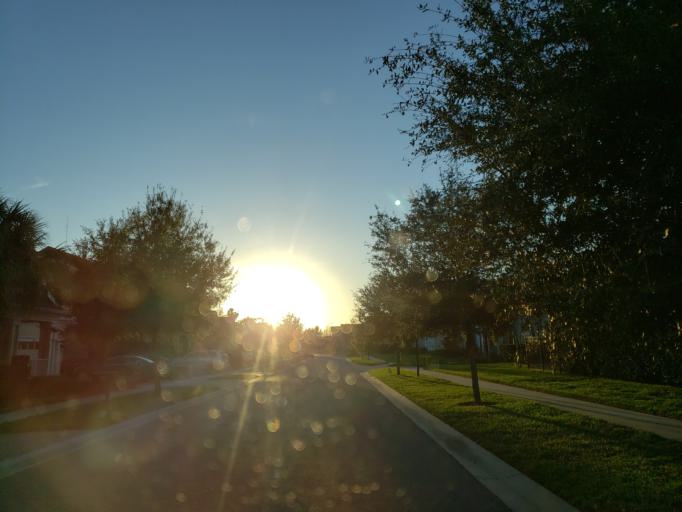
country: US
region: Florida
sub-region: Hillsborough County
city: Boyette
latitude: 27.8438
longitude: -82.2525
